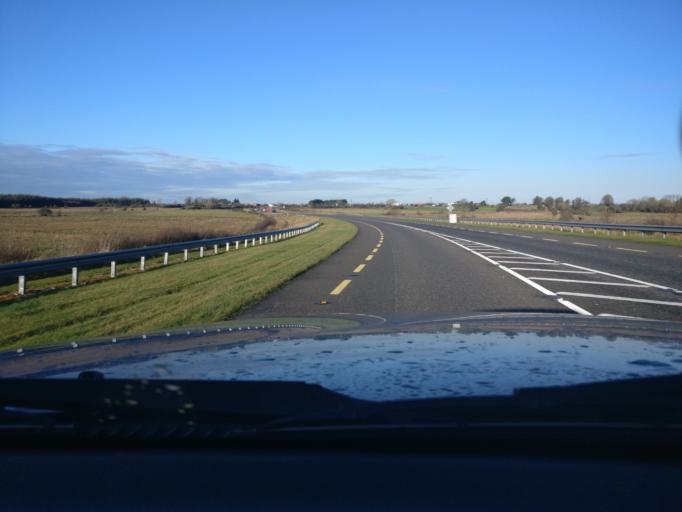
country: IE
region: Connaught
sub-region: County Galway
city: Loughrea
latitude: 53.2549
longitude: -8.5974
